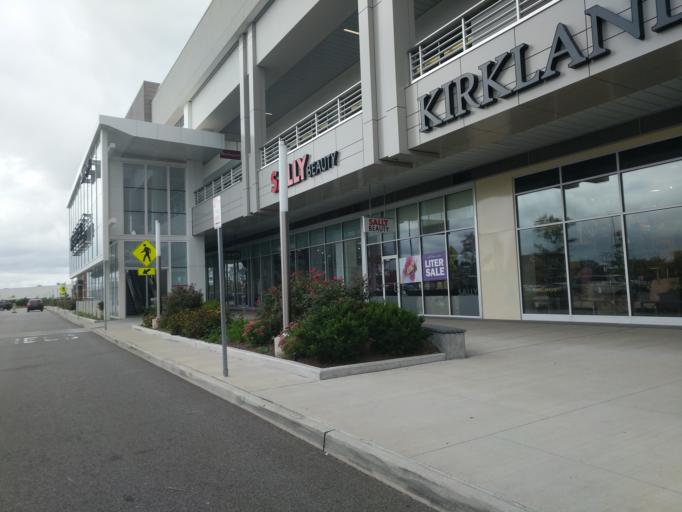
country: US
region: New York
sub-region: Nassau County
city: South Valley Stream
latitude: 40.6636
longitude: -73.7268
